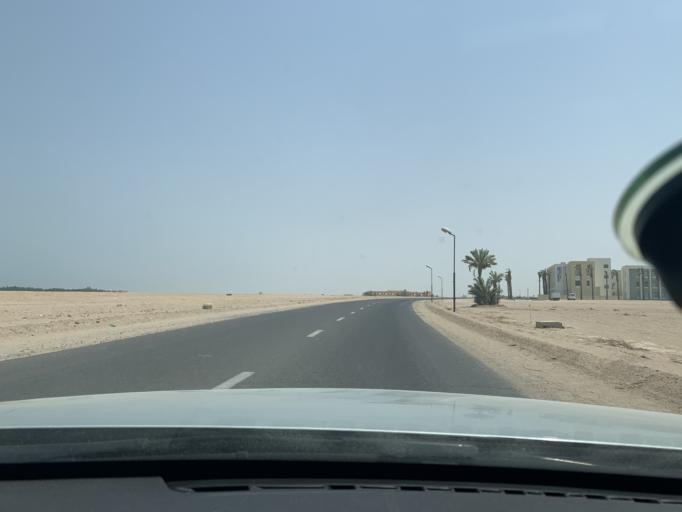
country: EG
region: Red Sea
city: El Gouna
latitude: 27.3709
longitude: 33.6633
